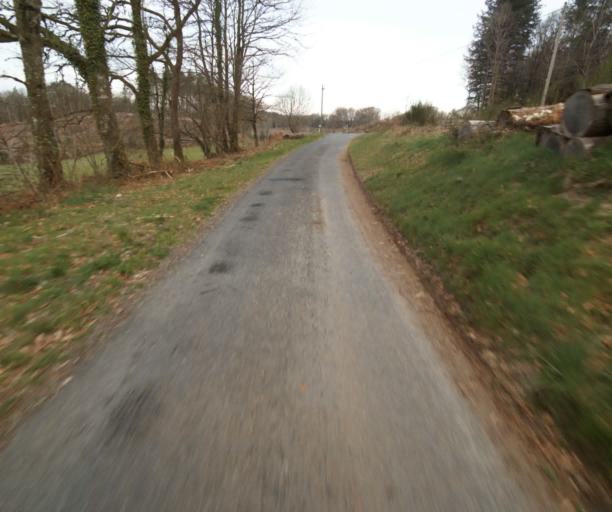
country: FR
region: Limousin
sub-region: Departement de la Correze
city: Correze
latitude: 45.4232
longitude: 1.8674
